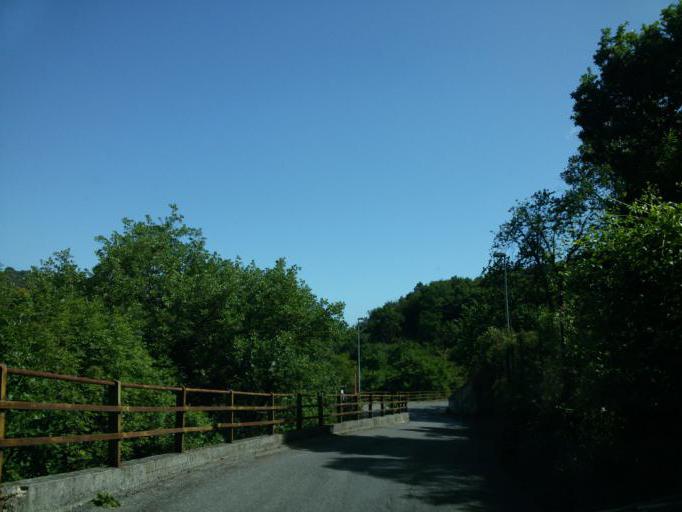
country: IT
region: Liguria
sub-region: Provincia di Genova
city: Genoa
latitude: 44.4307
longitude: 8.9453
